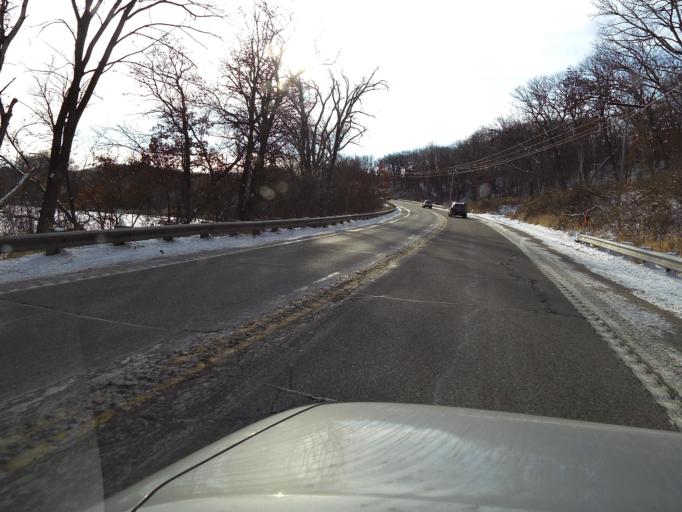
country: US
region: Minnesota
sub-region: Dakota County
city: Inver Grove Heights
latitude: 44.8235
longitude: -93.0832
